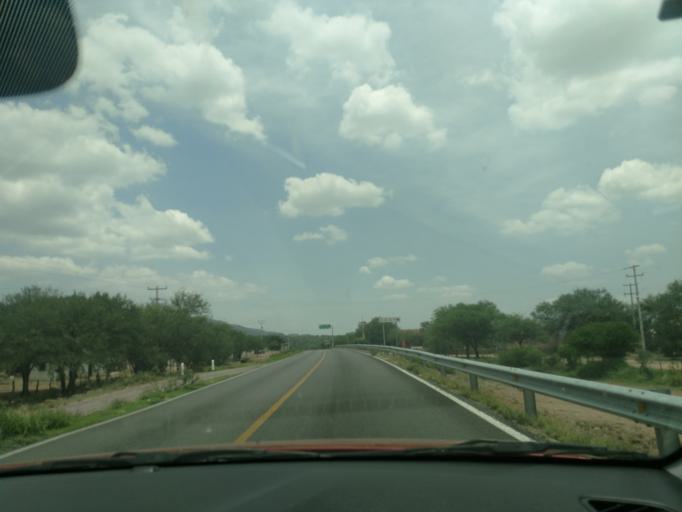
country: MX
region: San Luis Potosi
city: Villa Juarez
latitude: 22.0185
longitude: -100.3880
